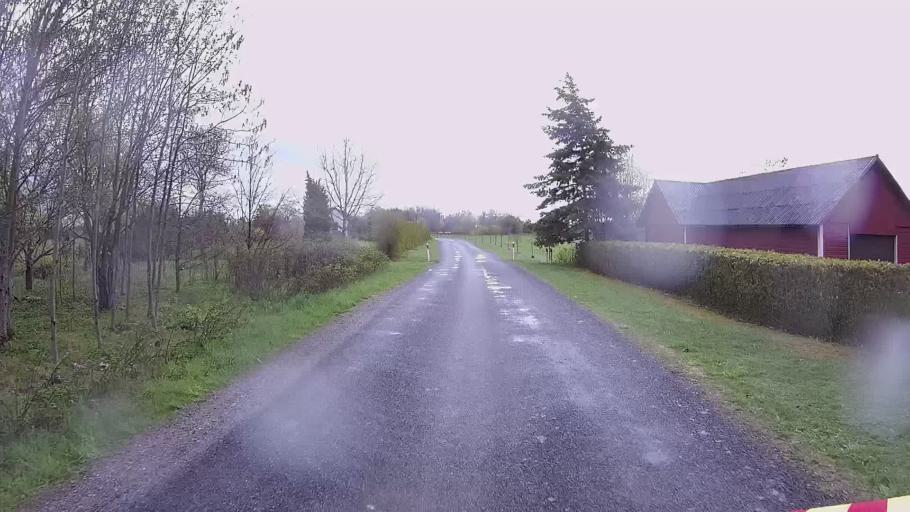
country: EE
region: Hiiumaa
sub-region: Kaerdla linn
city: Kardla
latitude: 58.6972
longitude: 22.5658
